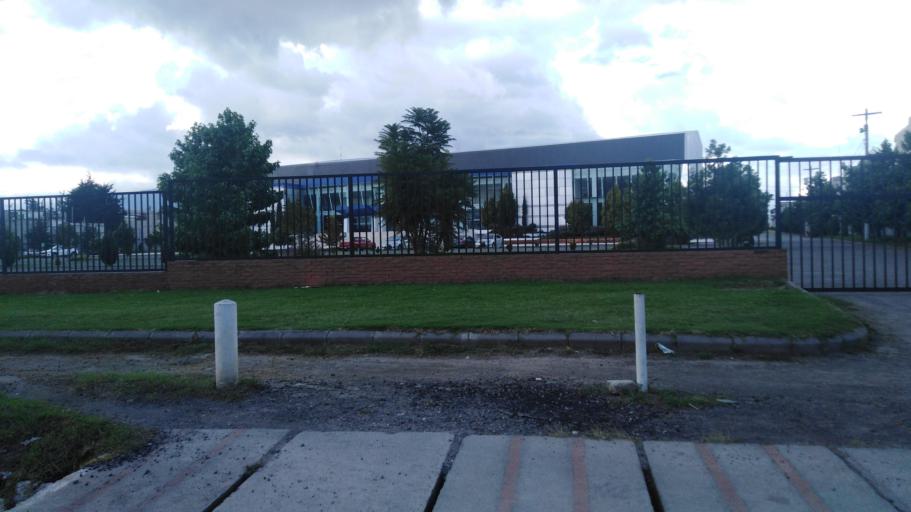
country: GT
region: Quetzaltenango
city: Olintepeque
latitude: 14.8613
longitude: -91.5121
